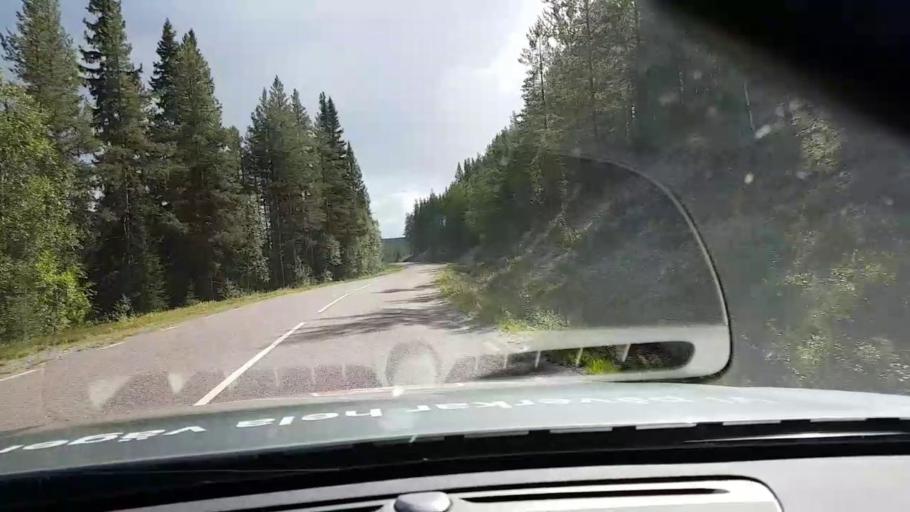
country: SE
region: Vaesterbotten
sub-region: Asele Kommun
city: Asele
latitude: 63.8764
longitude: 17.3568
